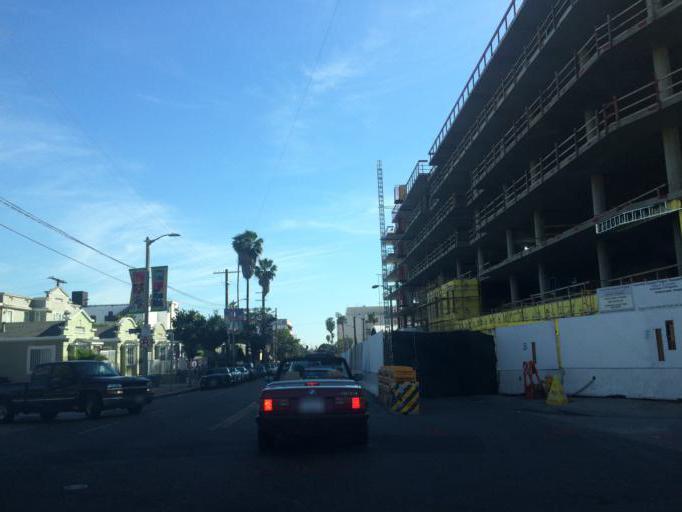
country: US
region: California
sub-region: Los Angeles County
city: Hollywood
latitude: 34.0999
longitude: -118.3223
